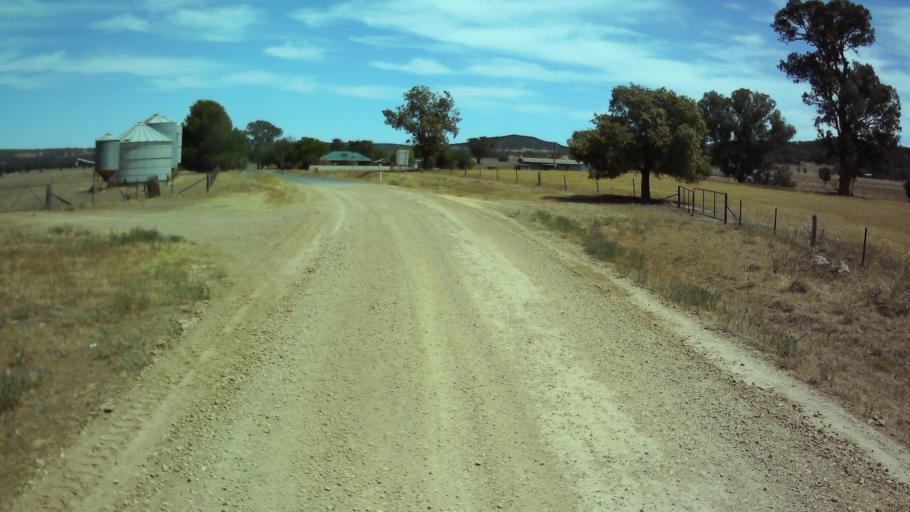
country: AU
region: New South Wales
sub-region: Weddin
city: Grenfell
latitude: -33.8316
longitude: 148.1745
